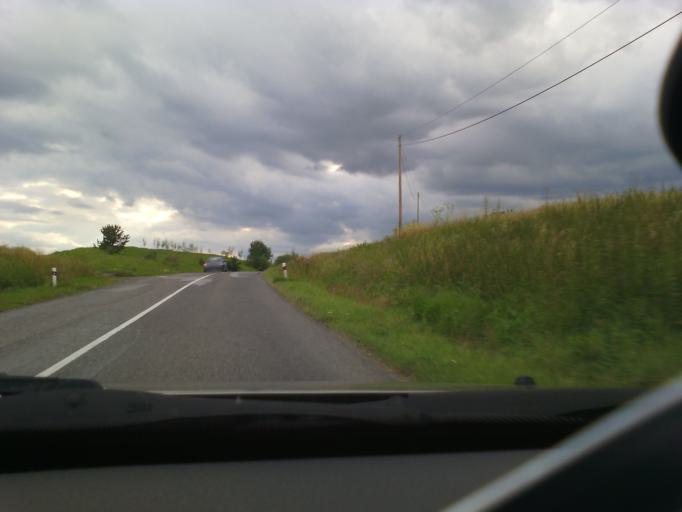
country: SK
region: Presovsky
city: Lubica
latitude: 49.0842
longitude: 20.4118
